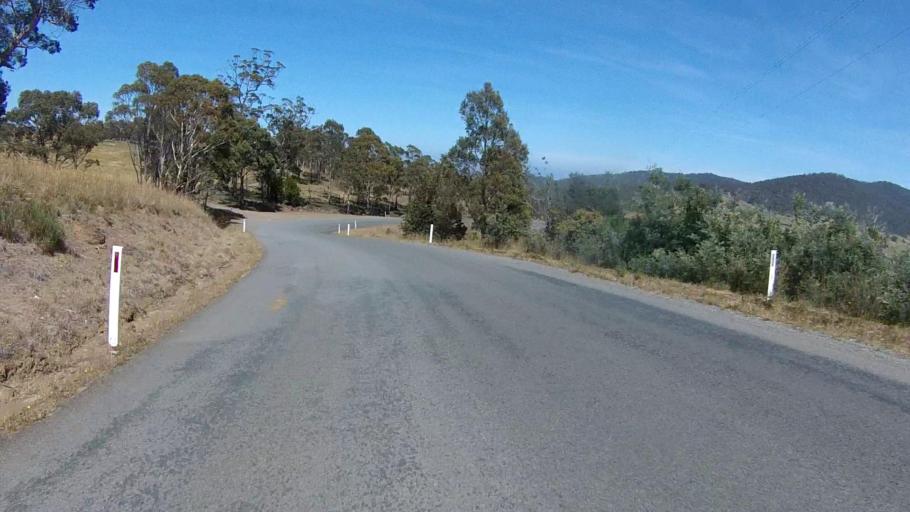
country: AU
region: Tasmania
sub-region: Sorell
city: Sorell
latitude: -42.7429
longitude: 147.7338
